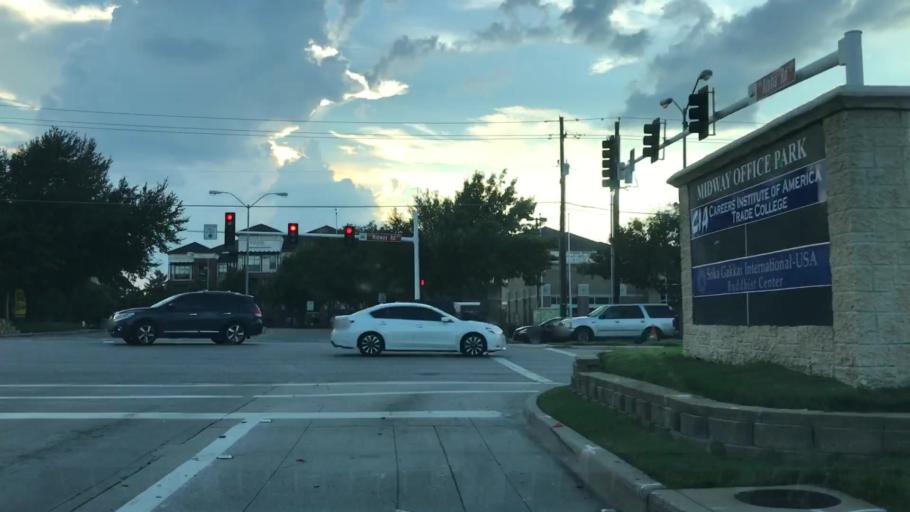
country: US
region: Texas
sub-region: Dallas County
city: Addison
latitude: 32.9332
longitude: -96.8388
